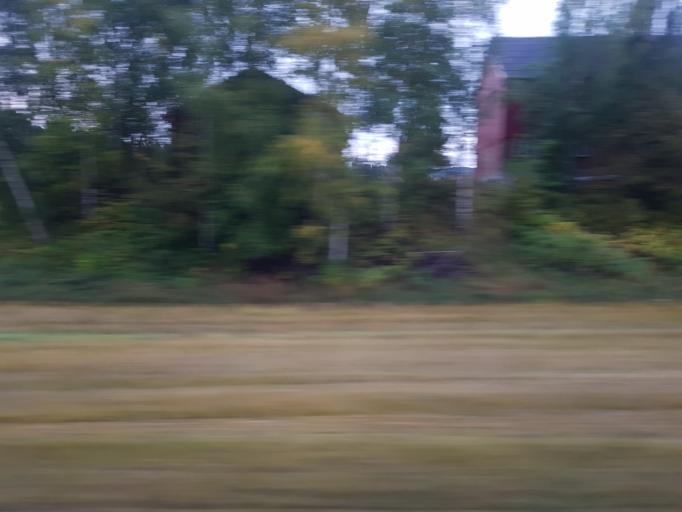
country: NO
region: Sor-Trondelag
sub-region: Melhus
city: Lundamo
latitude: 63.1265
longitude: 10.2468
